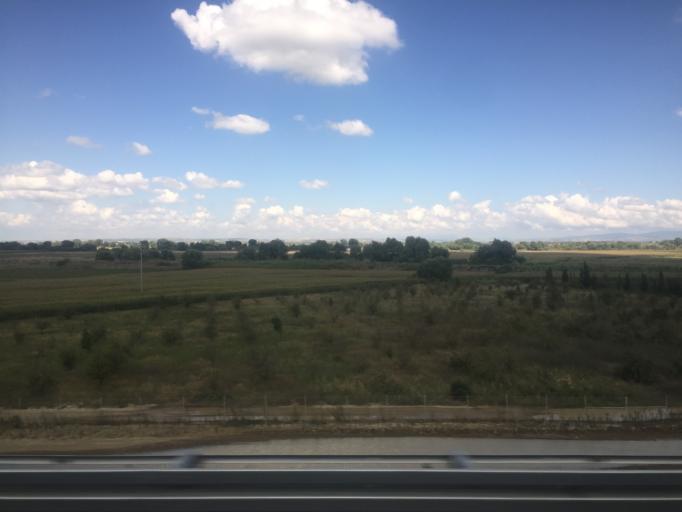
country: TR
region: Bursa
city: Karacabey
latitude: 40.1235
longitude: 28.2831
